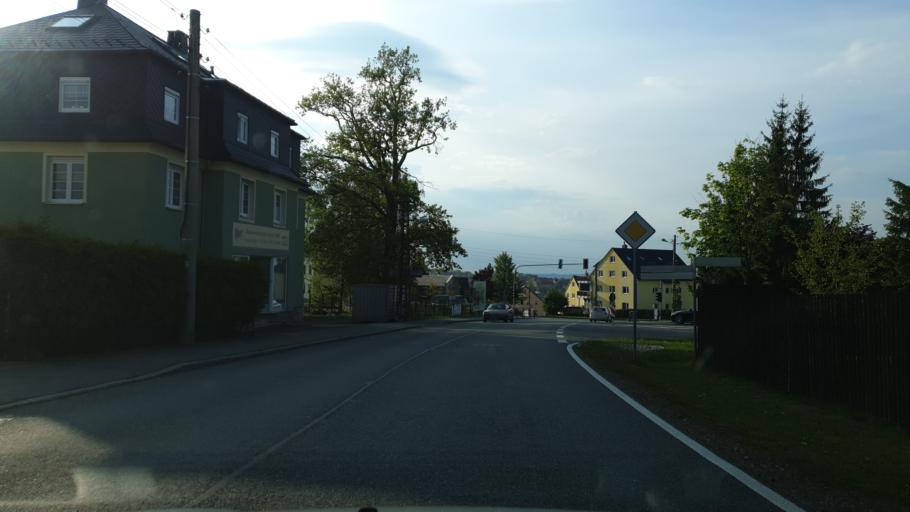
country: DE
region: Saxony
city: Stollberg
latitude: 50.7037
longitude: 12.7868
